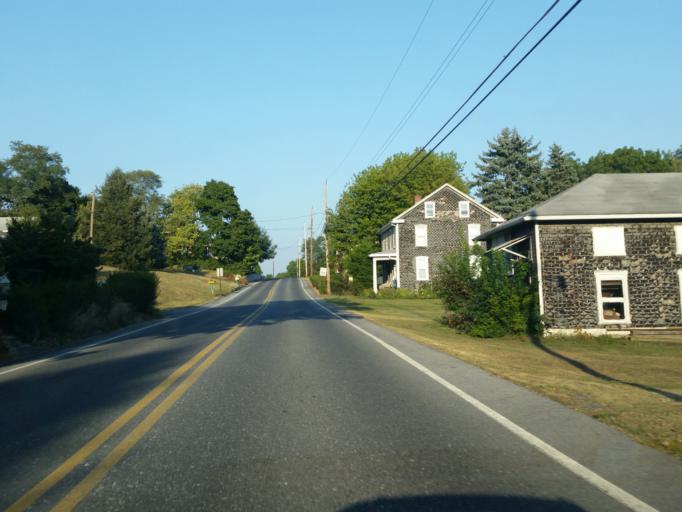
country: US
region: Pennsylvania
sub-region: Lebanon County
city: Annville
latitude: 40.3388
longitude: -76.5344
